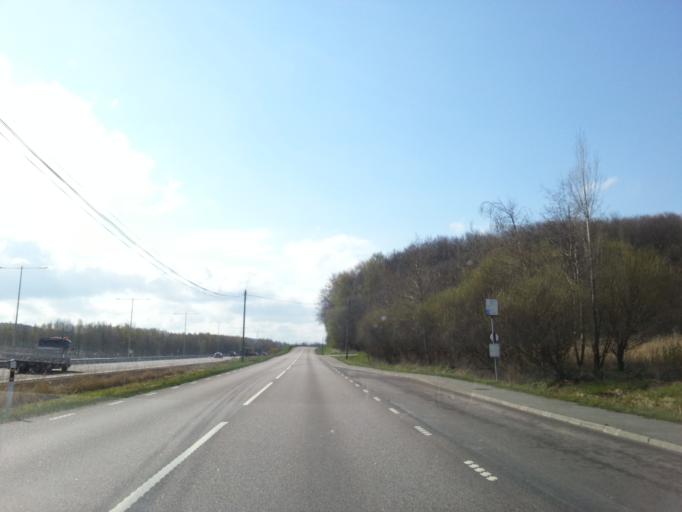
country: SE
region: Vaestra Goetaland
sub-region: Ale Kommun
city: Surte
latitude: 57.8414
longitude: 12.0050
